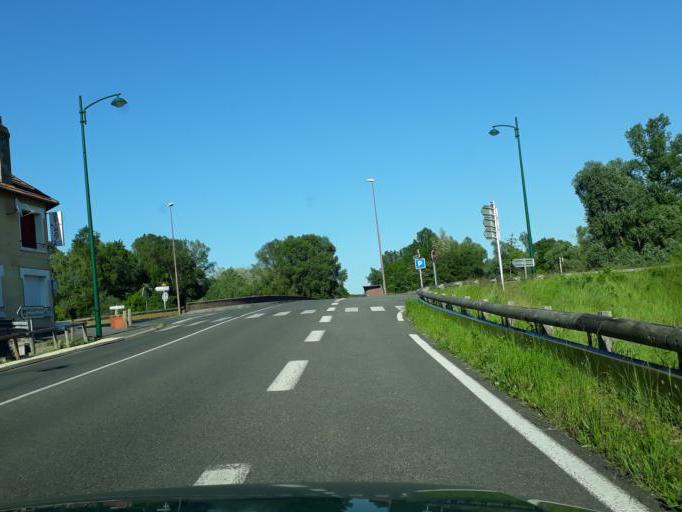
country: FR
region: Bourgogne
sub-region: Departement de la Nievre
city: Cosne-Cours-sur-Loire
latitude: 47.4111
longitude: 2.9059
